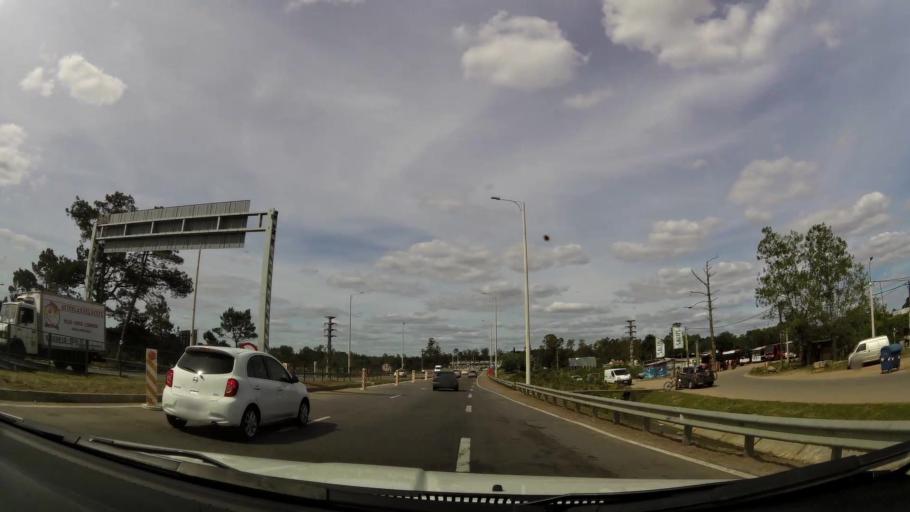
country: UY
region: Canelones
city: Empalme Olmos
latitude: -34.7876
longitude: -55.8923
